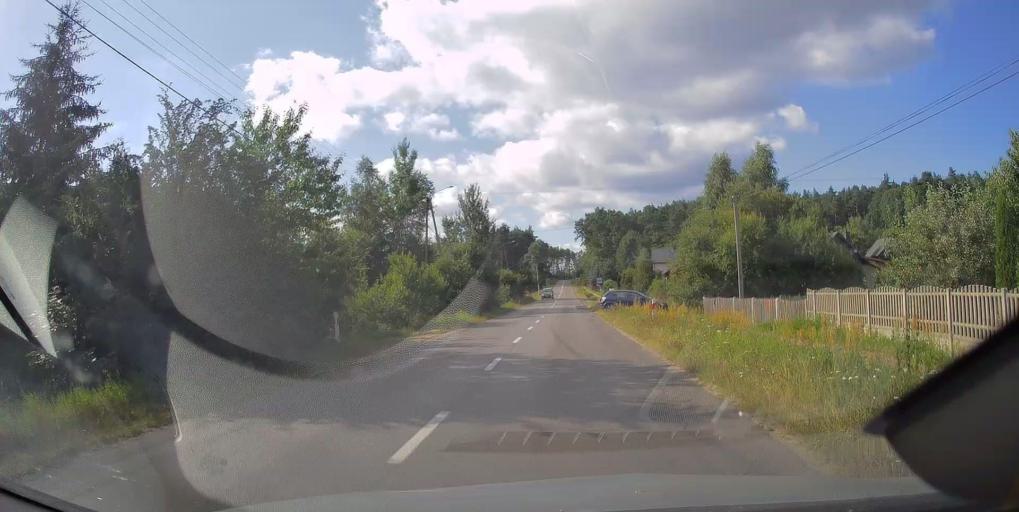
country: PL
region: Swietokrzyskie
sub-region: Powiat skarzyski
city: Suchedniow
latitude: 51.0092
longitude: 20.8433
